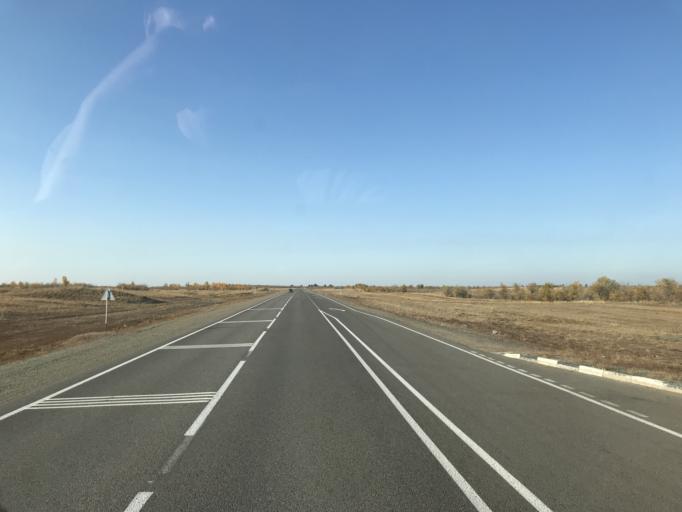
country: KZ
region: Pavlodar
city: Koktobe
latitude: 51.8162
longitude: 77.4697
